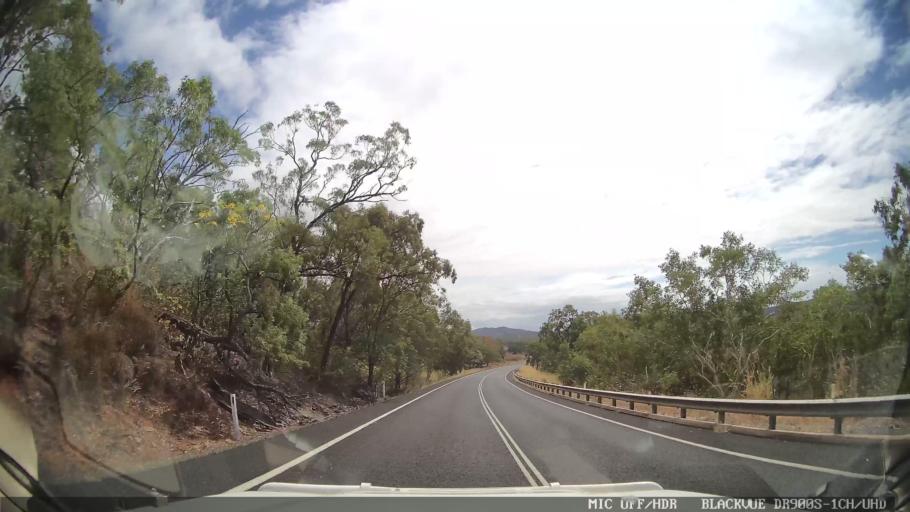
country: AU
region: Queensland
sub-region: Cook
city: Cooktown
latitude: -15.6471
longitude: 145.2211
